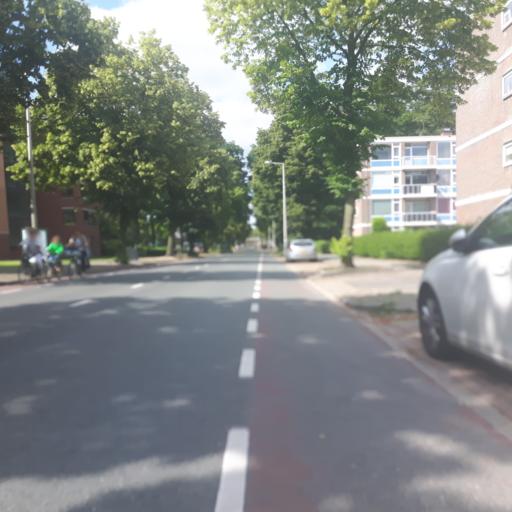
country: NL
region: Overijssel
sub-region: Gemeente Enschede
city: Enschede
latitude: 52.2082
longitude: 6.8809
